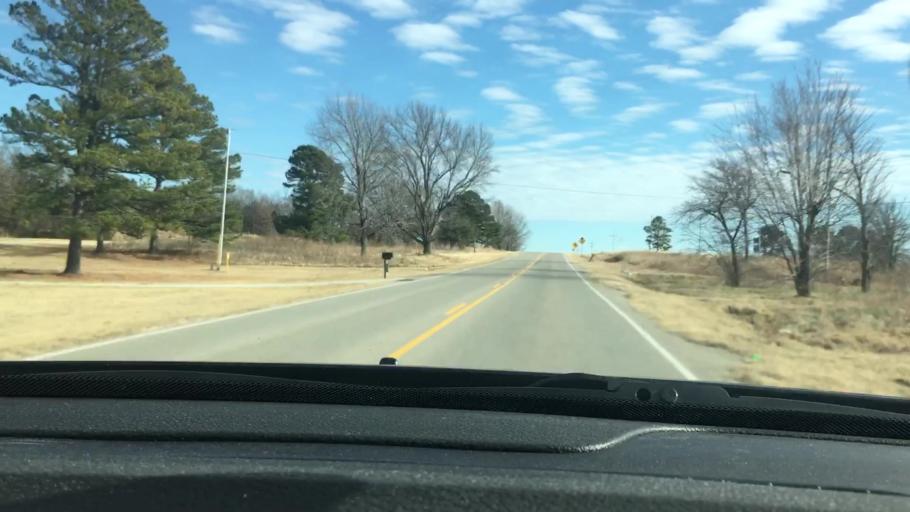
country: US
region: Oklahoma
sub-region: Pontotoc County
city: Ada
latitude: 34.7842
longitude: -96.7887
